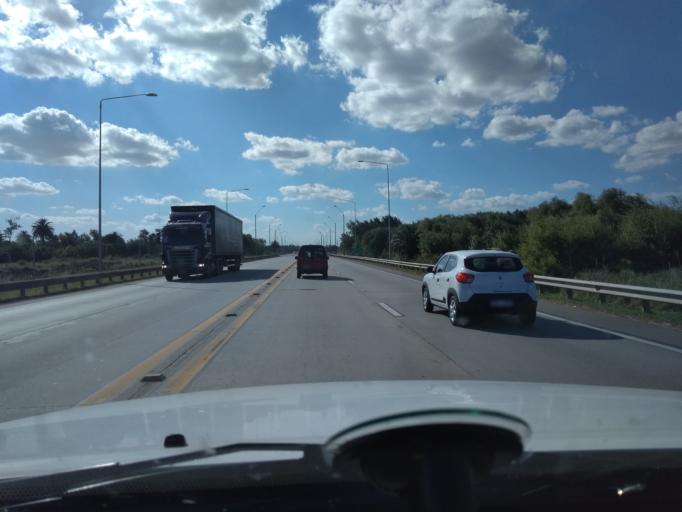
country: UY
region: Canelones
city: La Paz
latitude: -34.7777
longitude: -56.2627
